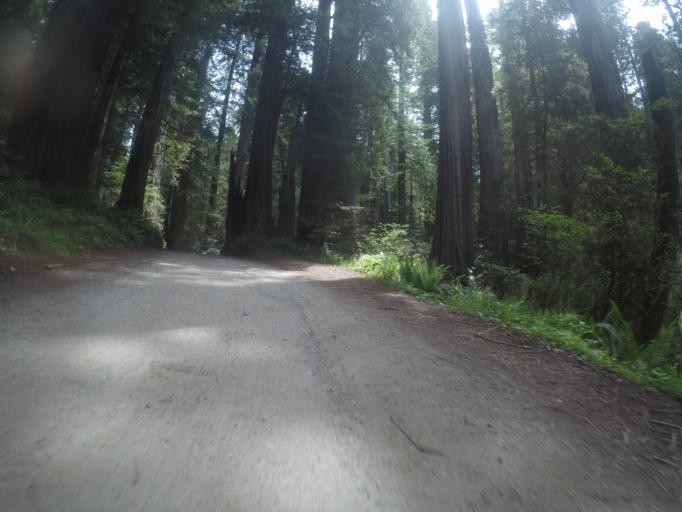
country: US
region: California
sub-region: Del Norte County
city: Bertsch-Oceanview
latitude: 41.7661
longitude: -124.1130
